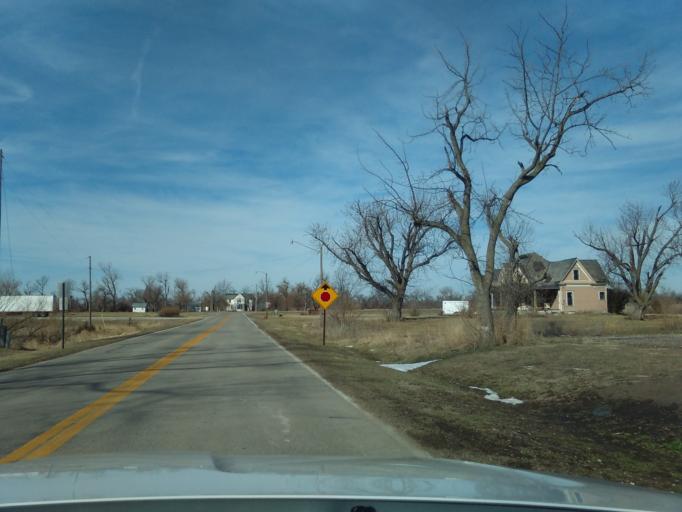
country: US
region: Nebraska
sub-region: Saline County
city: Friend
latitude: 40.7784
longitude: -97.2897
